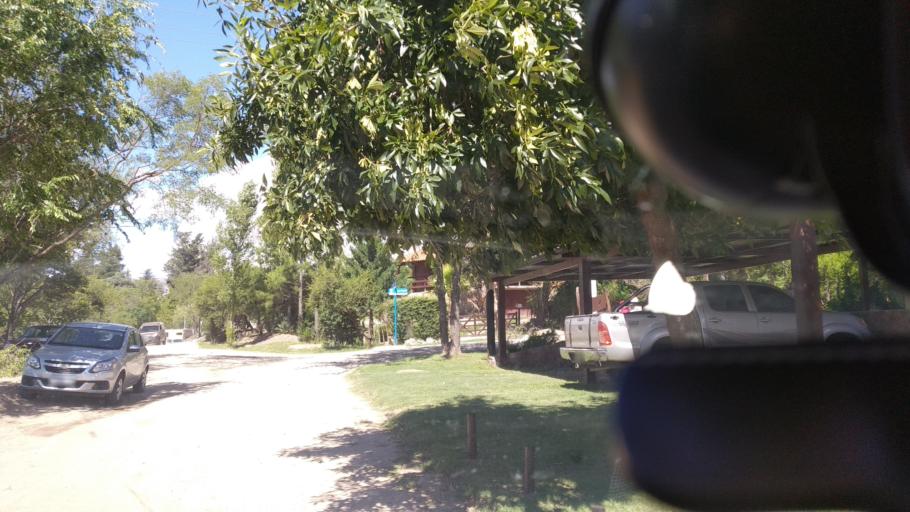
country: AR
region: Cordoba
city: Mina Clavero
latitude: -31.7226
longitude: -65.0114
